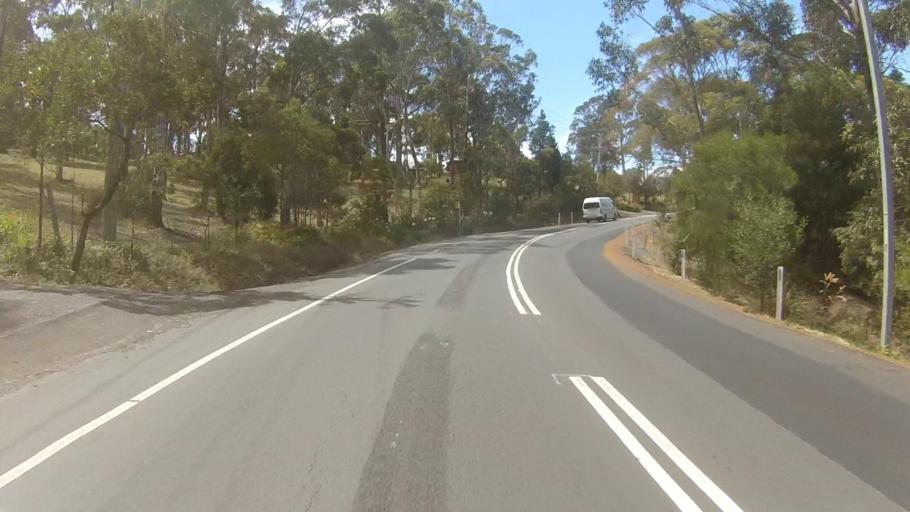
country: AU
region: Tasmania
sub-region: Kingborough
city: Kingston Beach
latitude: -42.9713
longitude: 147.3287
